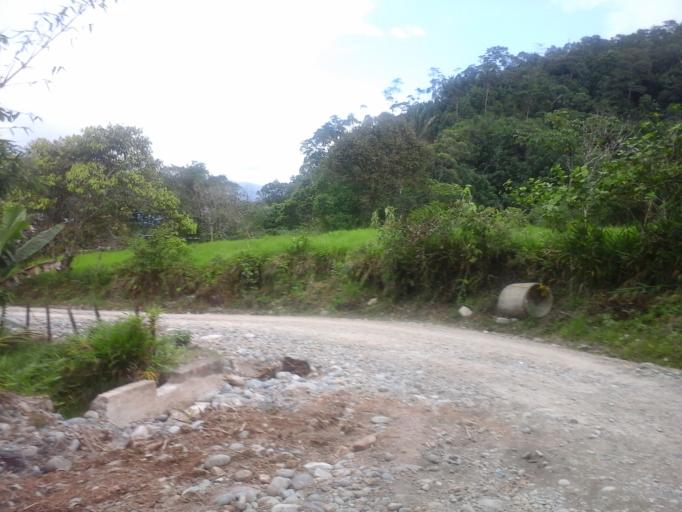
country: CO
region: Putumayo
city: Mocoa
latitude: 1.1823
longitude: -76.6722
